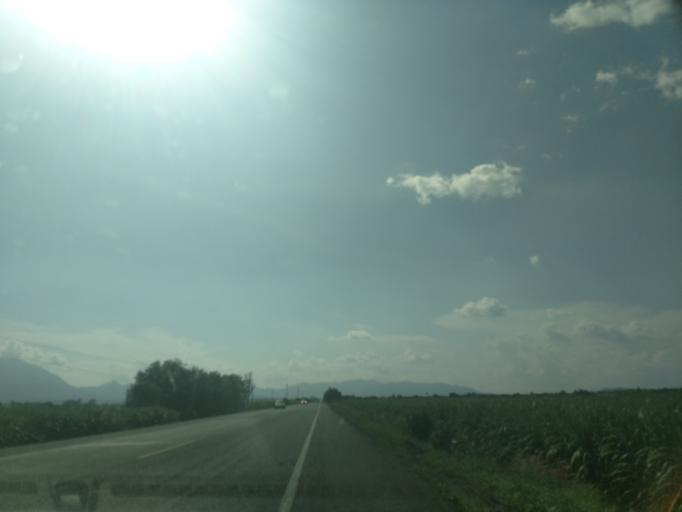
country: MX
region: Jalisco
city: Teuchitlan
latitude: 20.6827
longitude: -103.8611
